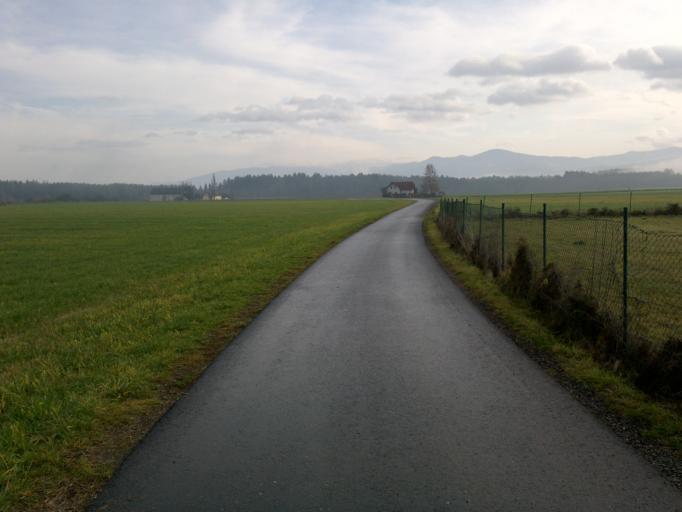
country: AT
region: Styria
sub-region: Politischer Bezirk Murtal
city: Judenburg
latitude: 47.1728
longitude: 14.6907
